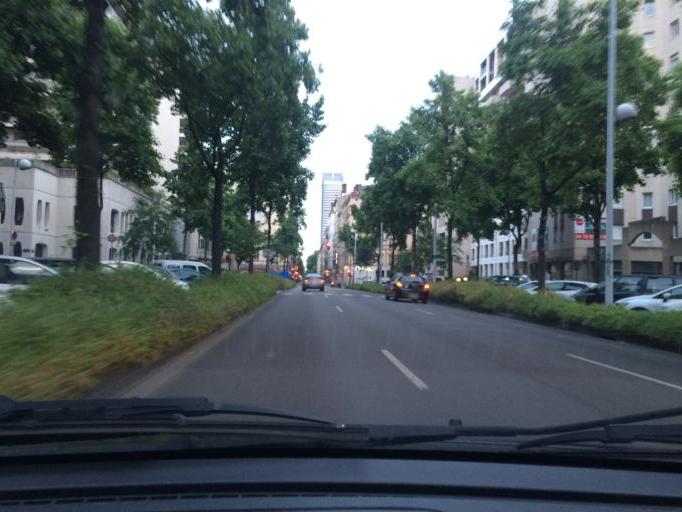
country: FR
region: Rhone-Alpes
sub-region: Departement du Rhone
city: Caluire-et-Cuire
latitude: 45.7713
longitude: 4.8502
